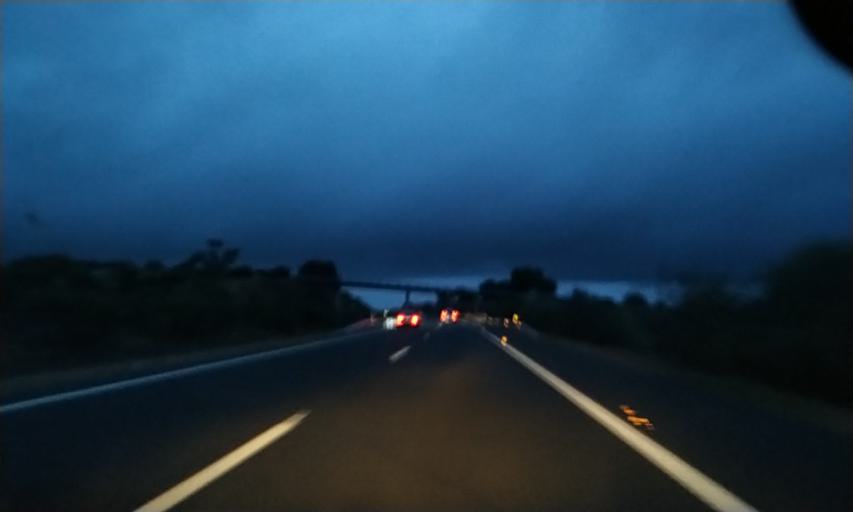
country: ES
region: Extremadura
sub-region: Provincia de Caceres
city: Aldea del Cano
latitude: 39.3123
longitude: -6.3274
